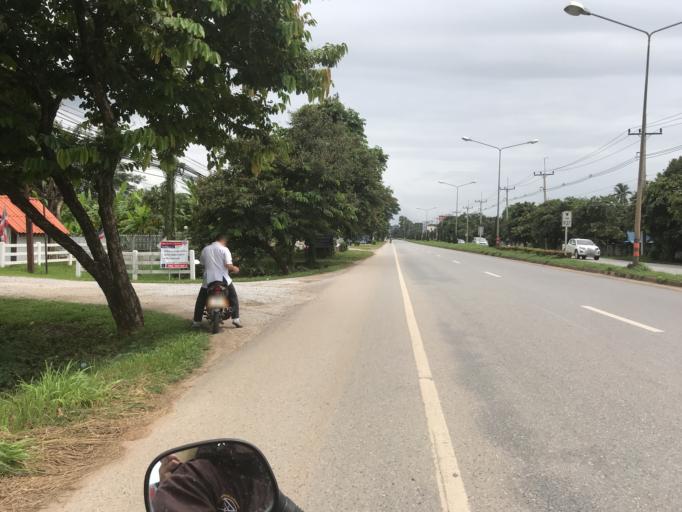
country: TH
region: Chiang Rai
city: Chiang Rai
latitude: 19.9448
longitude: 99.8471
